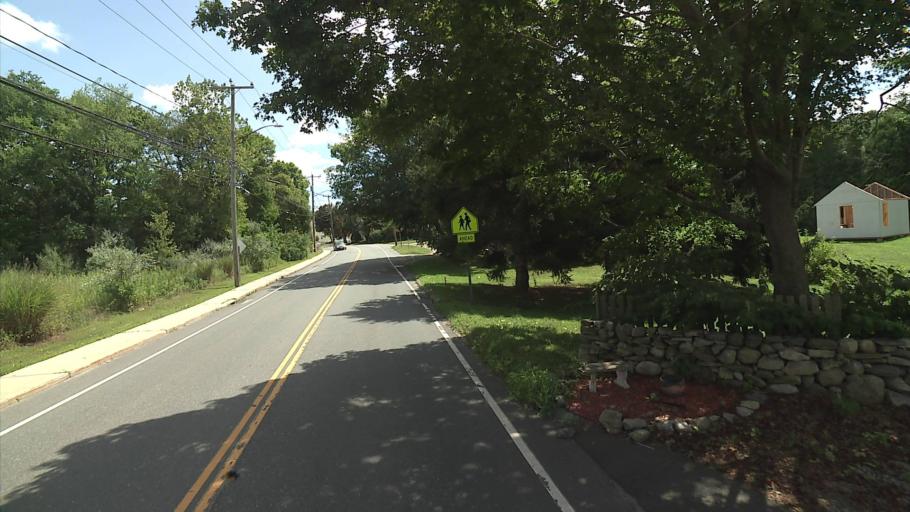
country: US
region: Connecticut
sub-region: New London County
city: Mystic
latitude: 41.3534
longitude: -71.9842
